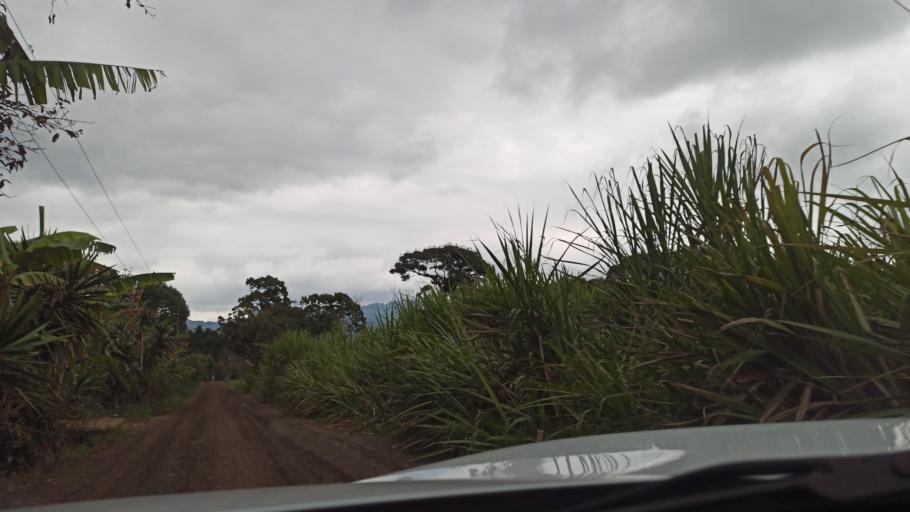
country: MX
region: Veracruz
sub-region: Chocaman
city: San Jose Neria
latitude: 18.9828
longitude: -97.0097
